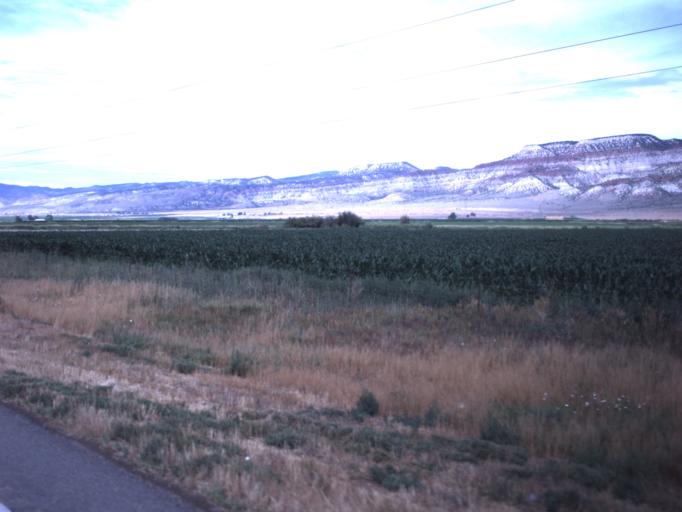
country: US
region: Utah
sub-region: Sevier County
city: Richfield
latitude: 38.8265
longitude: -111.9952
